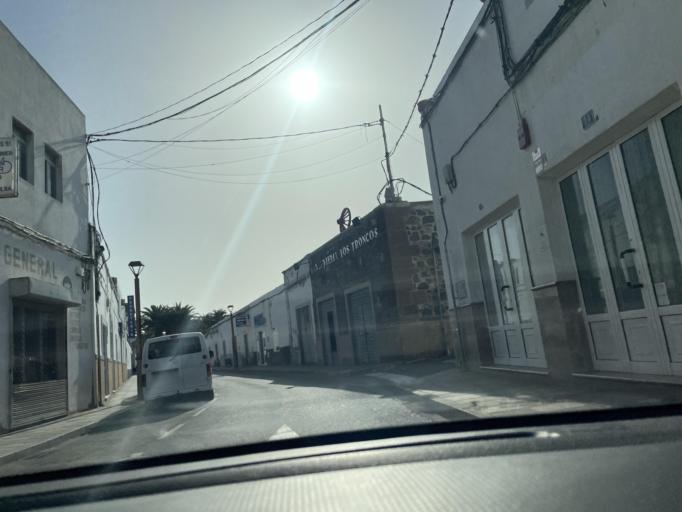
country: ES
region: Canary Islands
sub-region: Provincia de Las Palmas
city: Arrecife
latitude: 28.9647
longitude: -13.5411
